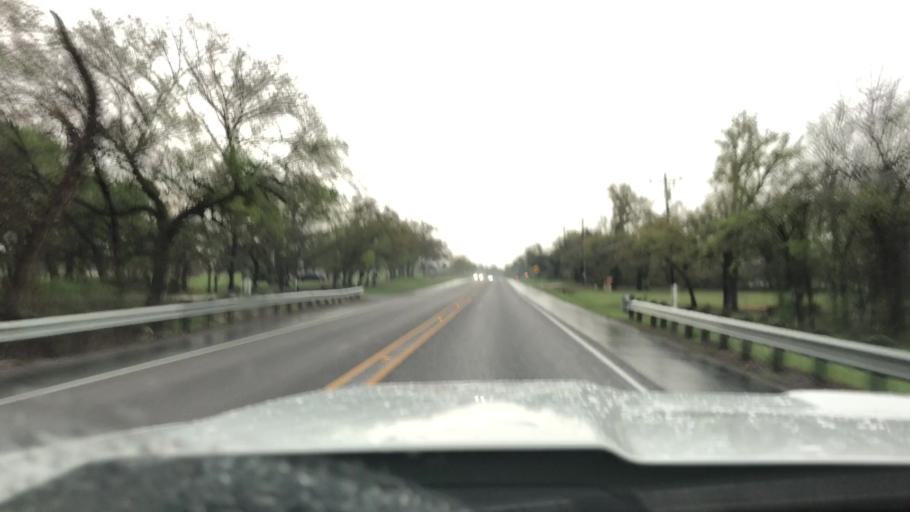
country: US
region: Texas
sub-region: Johnson County
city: Keene
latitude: 32.4374
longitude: -97.3106
